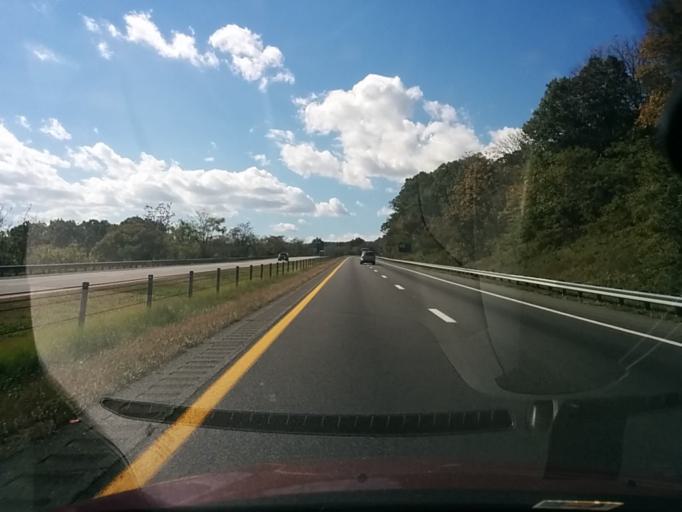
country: US
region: Virginia
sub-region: City of Waynesboro
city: Waynesboro
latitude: 38.0417
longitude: -78.8256
